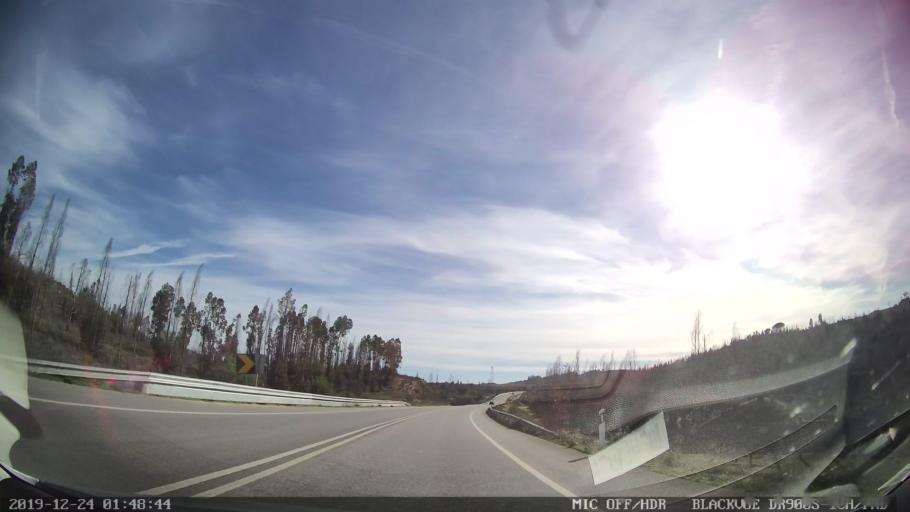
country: PT
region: Portalegre
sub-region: Nisa
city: Nisa
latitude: 39.5189
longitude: -7.7706
